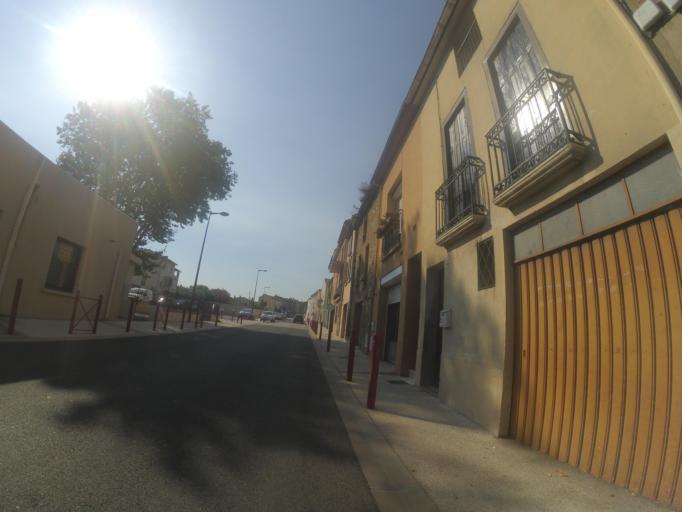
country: FR
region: Languedoc-Roussillon
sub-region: Departement des Pyrenees-Orientales
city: Toulouges
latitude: 42.6700
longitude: 2.8308
